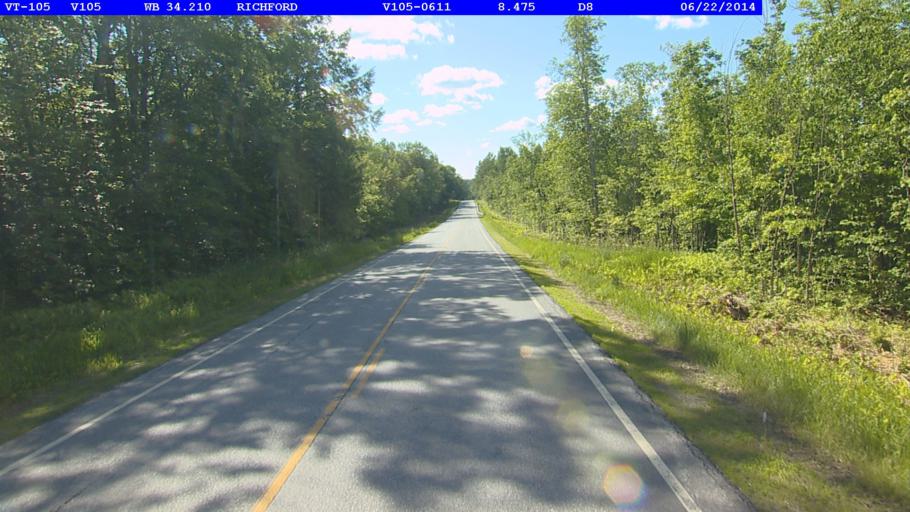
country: US
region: Vermont
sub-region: Franklin County
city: Richford
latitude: 44.9913
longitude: -72.5626
